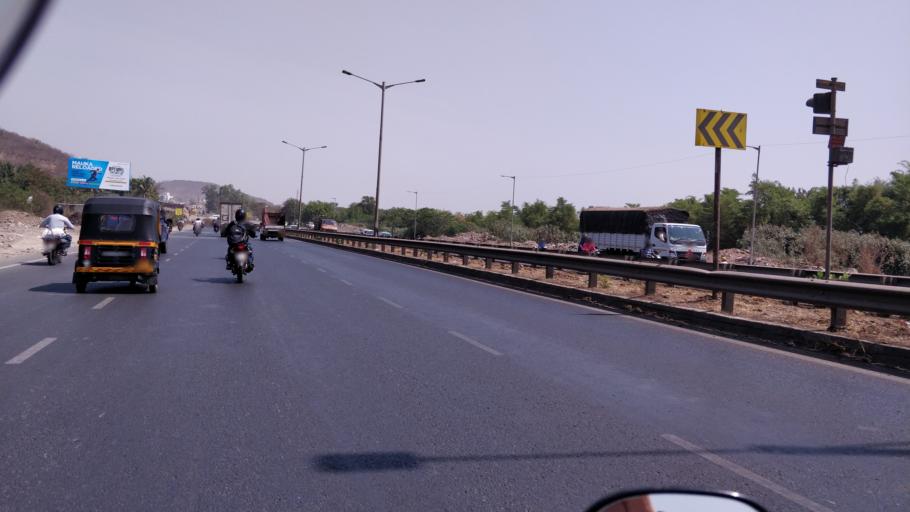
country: IN
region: Maharashtra
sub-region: Pune Division
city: Shivaji Nagar
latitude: 18.5301
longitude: 73.7788
